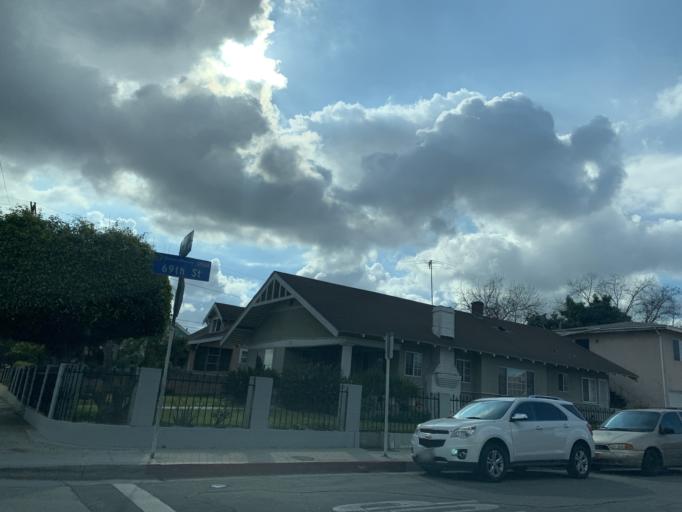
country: US
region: California
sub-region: Los Angeles County
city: Florence-Graham
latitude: 33.9773
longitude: -118.2413
